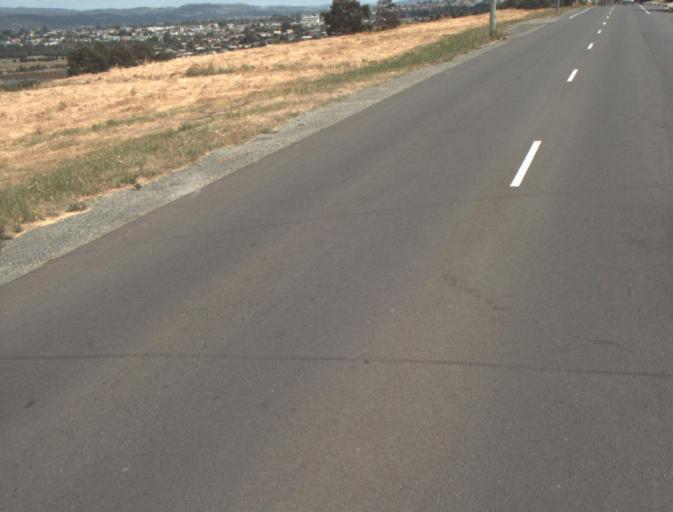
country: AU
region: Tasmania
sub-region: Launceston
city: Newstead
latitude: -41.4189
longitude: 147.1653
